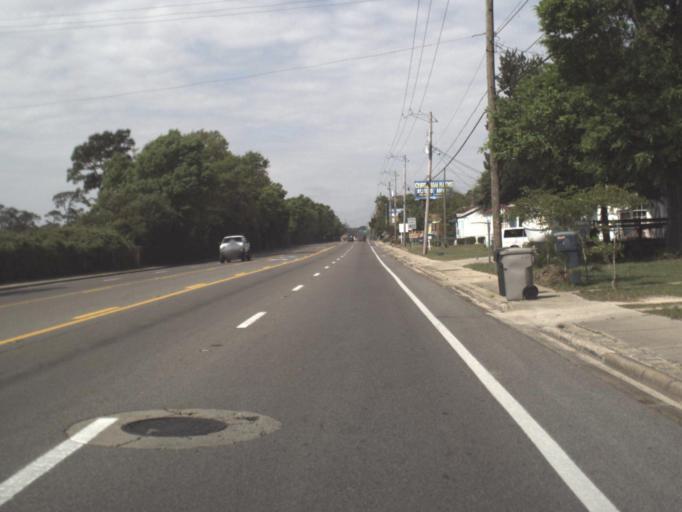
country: US
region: Florida
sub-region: Escambia County
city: Warrington
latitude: 30.3913
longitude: -87.2646
